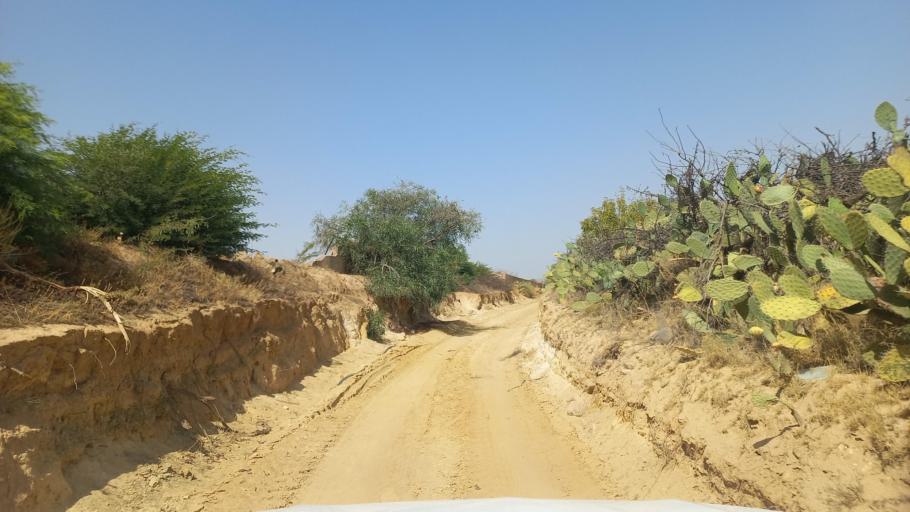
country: TN
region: Al Qasrayn
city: Kasserine
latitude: 35.2432
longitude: 9.0468
